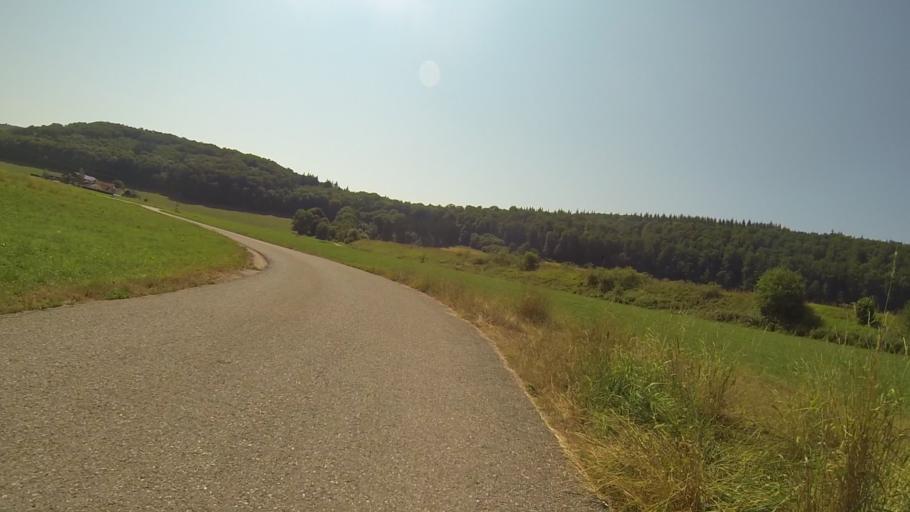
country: DE
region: Baden-Wuerttemberg
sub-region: Regierungsbezirk Stuttgart
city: Konigsbronn
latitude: 48.7305
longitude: 10.1421
